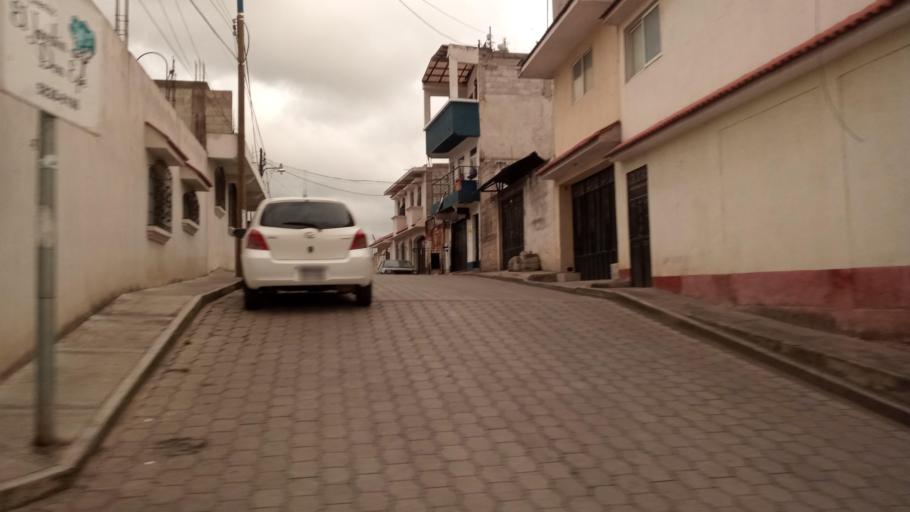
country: GT
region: Quetzaltenango
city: Quetzaltenango
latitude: 14.8291
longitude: -91.5296
